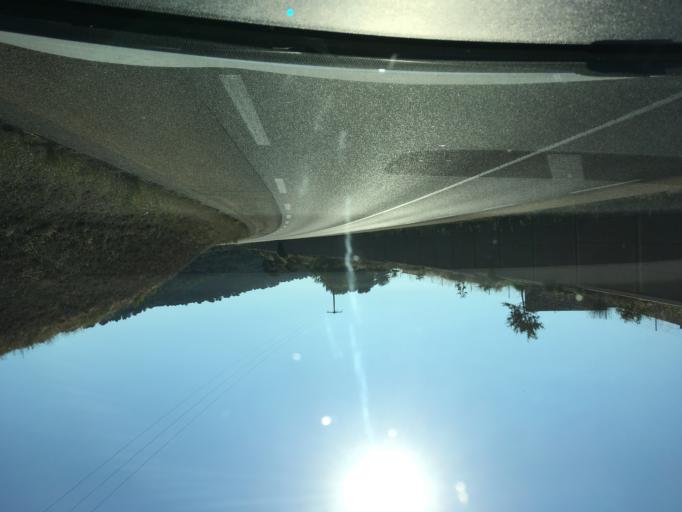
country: FR
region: Provence-Alpes-Cote d'Azur
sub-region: Departement des Bouches-du-Rhone
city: Charleval
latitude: 43.7158
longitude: 5.2483
